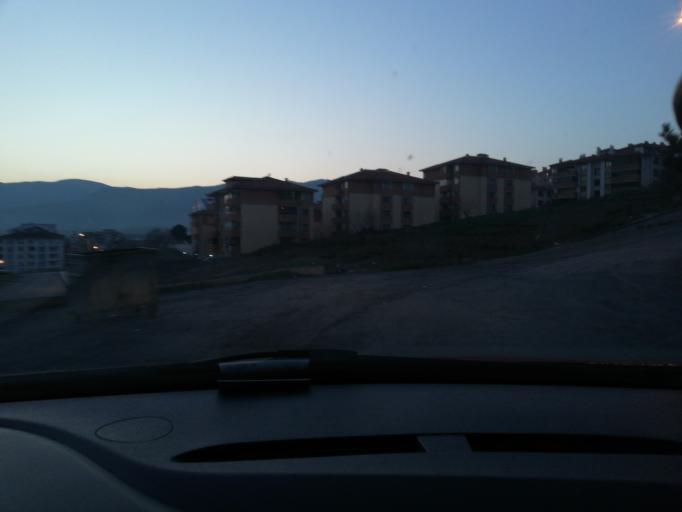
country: TR
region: Karabuk
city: Safranbolu
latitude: 41.2198
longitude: 32.6712
